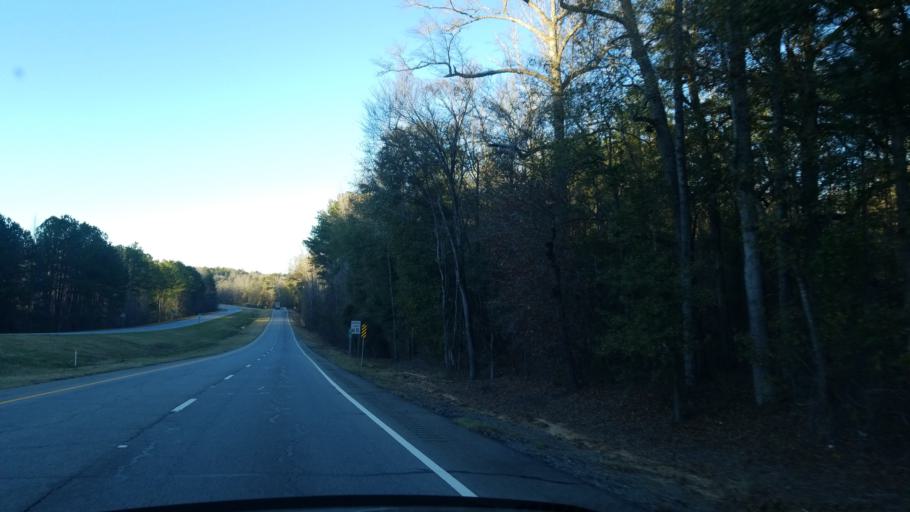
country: US
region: Georgia
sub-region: Chattahoochee County
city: Cusseta
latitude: 32.2467
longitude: -84.7193
